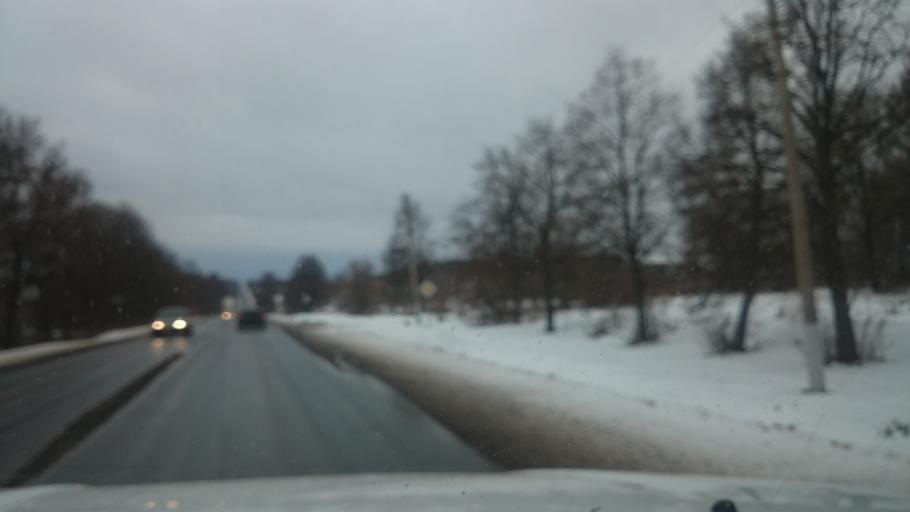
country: RU
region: Tula
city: Kosaya Gora
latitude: 54.1099
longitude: 37.5549
